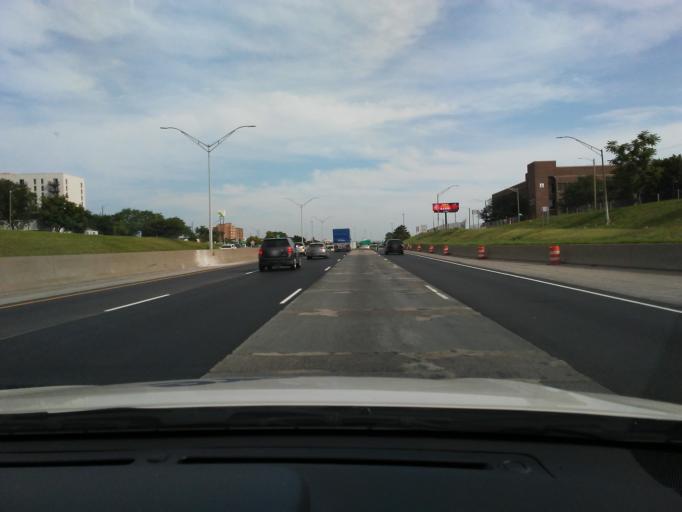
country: US
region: Michigan
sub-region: Wayne County
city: Detroit
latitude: 42.3576
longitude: -83.0520
